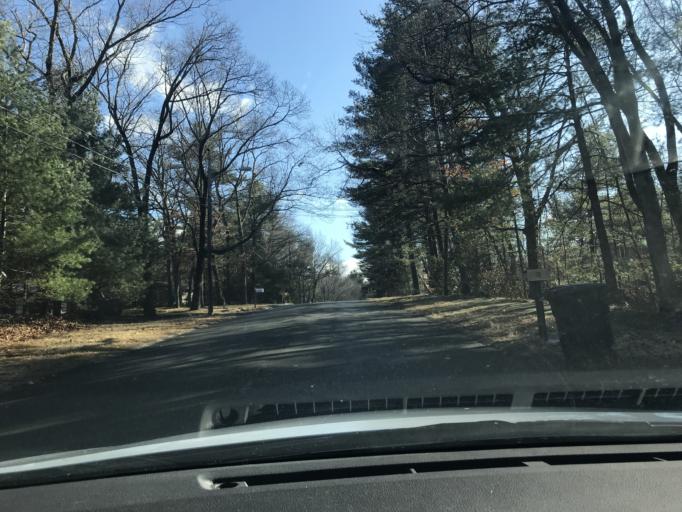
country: US
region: Massachusetts
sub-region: Middlesex County
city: Lexington
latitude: 42.4785
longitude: -71.2284
